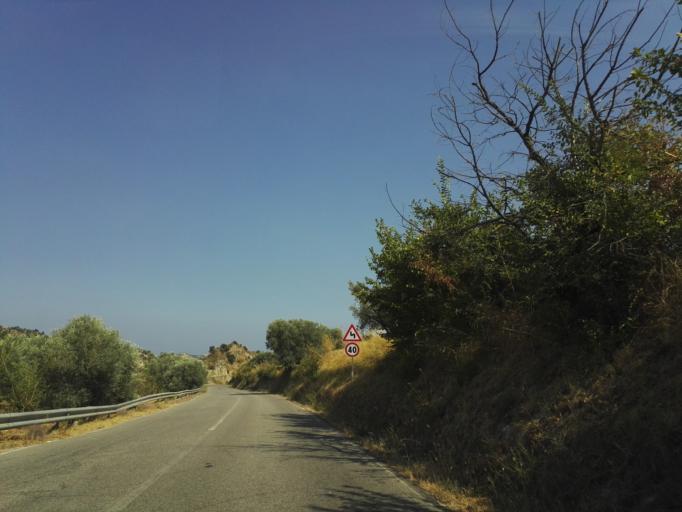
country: IT
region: Calabria
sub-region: Provincia di Reggio Calabria
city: Stilo
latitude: 38.4714
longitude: 16.4777
